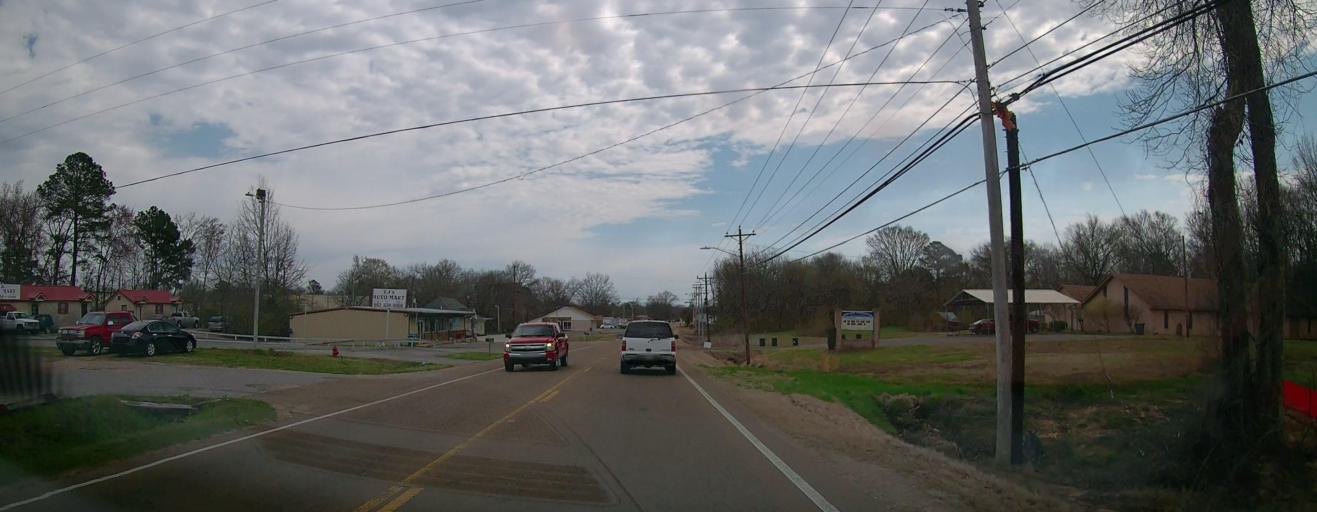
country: US
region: Mississippi
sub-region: Marshall County
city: Byhalia
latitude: 34.8725
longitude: -89.6942
